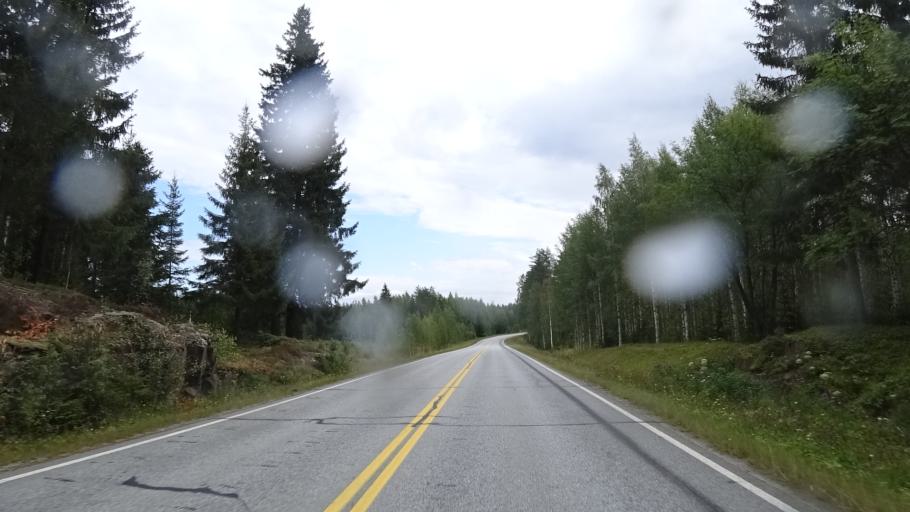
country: FI
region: North Karelia
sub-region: Keski-Karjala
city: Raeaekkylae
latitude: 62.1094
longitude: 29.7123
